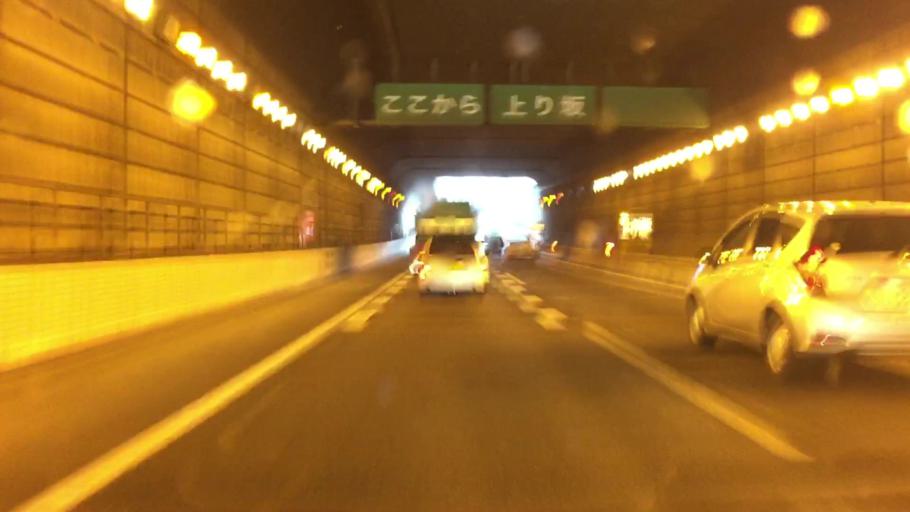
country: JP
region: Saitama
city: Wako
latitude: 35.7658
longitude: 139.6001
